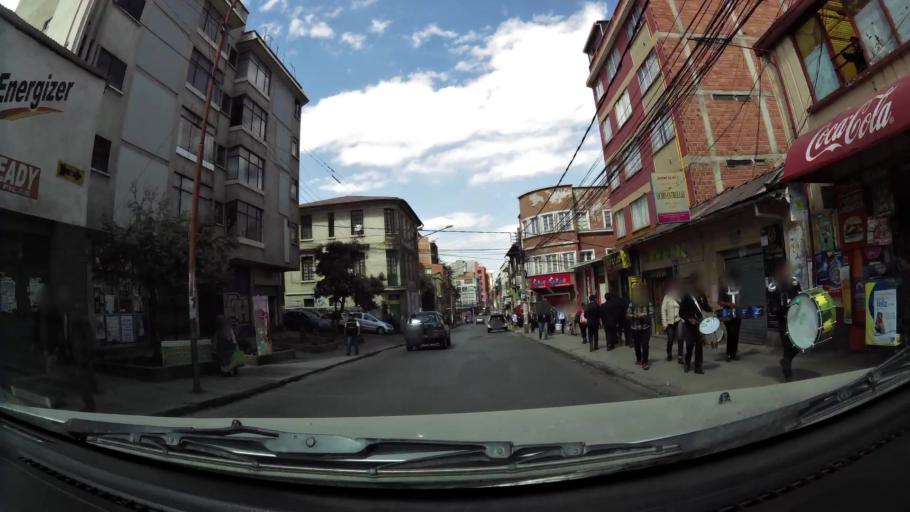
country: BO
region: La Paz
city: La Paz
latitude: -16.4908
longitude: -68.1369
